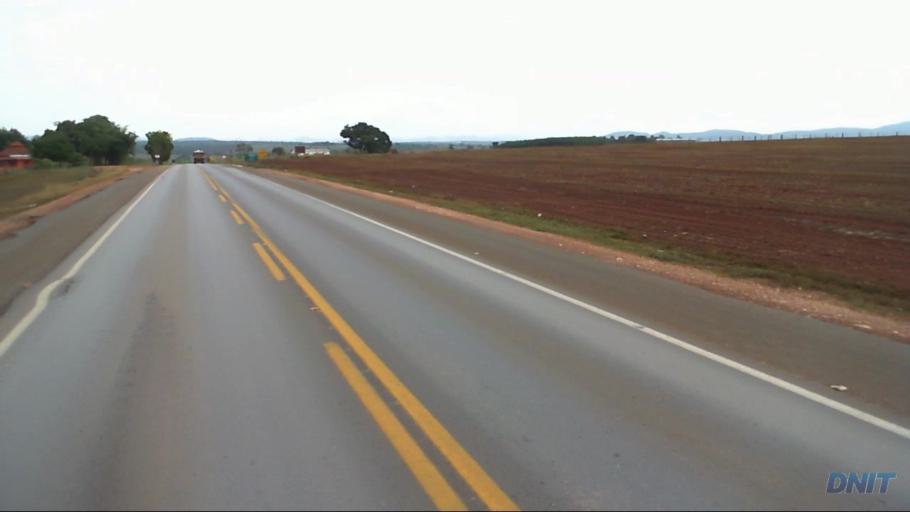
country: BR
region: Goias
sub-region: Uruacu
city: Uruacu
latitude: -14.6396
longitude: -49.1731
